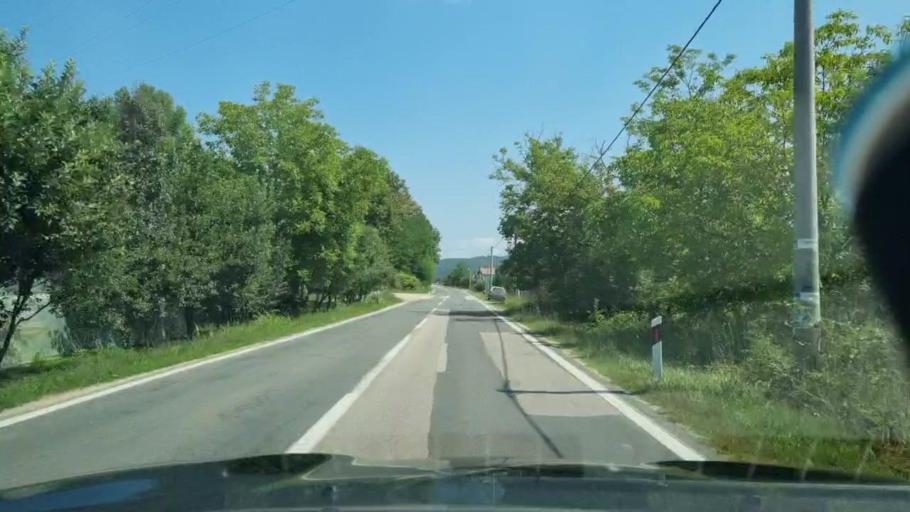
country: BA
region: Federation of Bosnia and Herzegovina
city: Sanski Most
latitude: 44.8059
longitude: 16.6437
